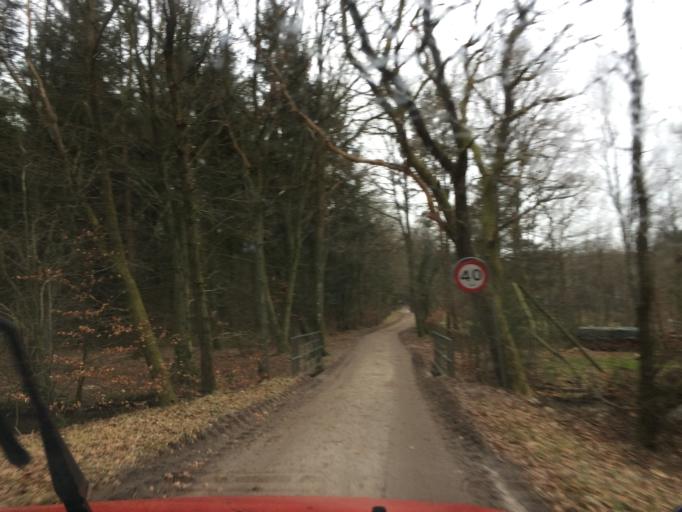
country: DK
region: Central Jutland
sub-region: Silkeborg Kommune
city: Virklund
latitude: 56.0281
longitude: 9.4946
